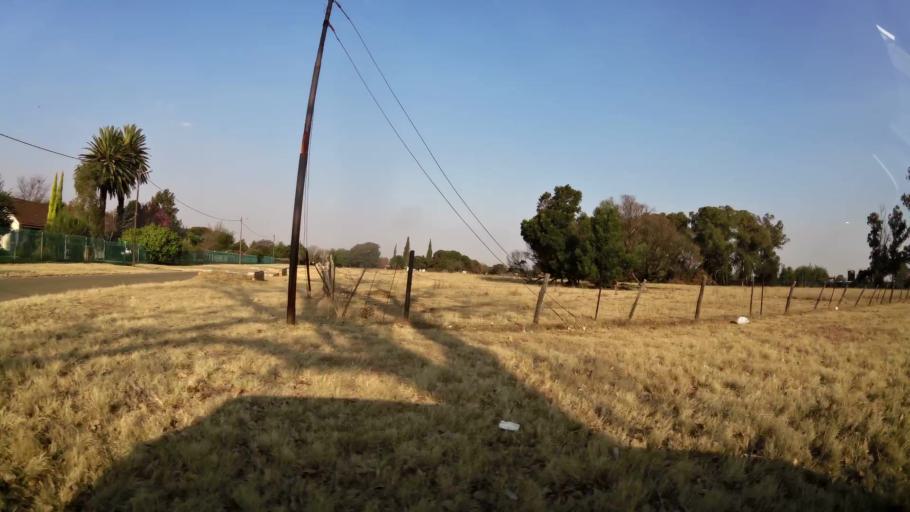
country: ZA
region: Gauteng
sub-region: Ekurhuleni Metropolitan Municipality
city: Benoni
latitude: -26.1461
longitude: 28.3750
